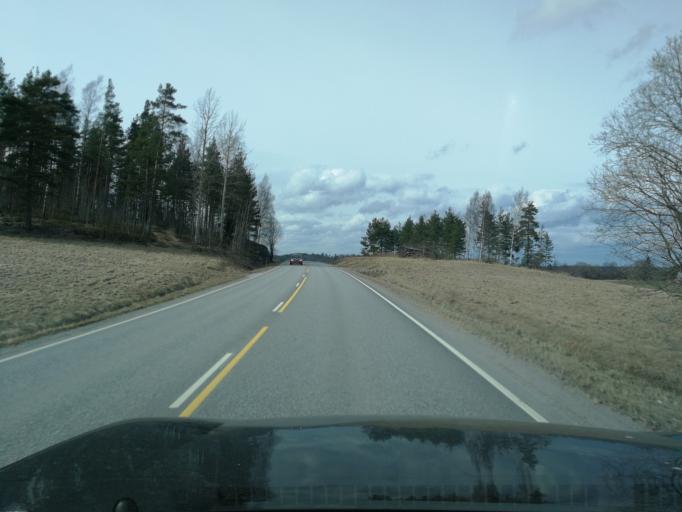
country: FI
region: Uusimaa
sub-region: Helsinki
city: Siuntio
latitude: 60.1081
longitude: 24.2452
